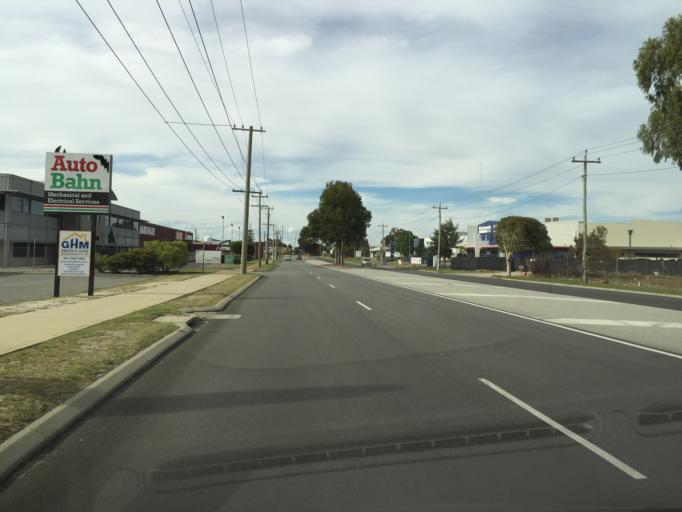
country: AU
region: Western Australia
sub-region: Canning
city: Canning Vale
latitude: -32.0630
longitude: 115.9036
